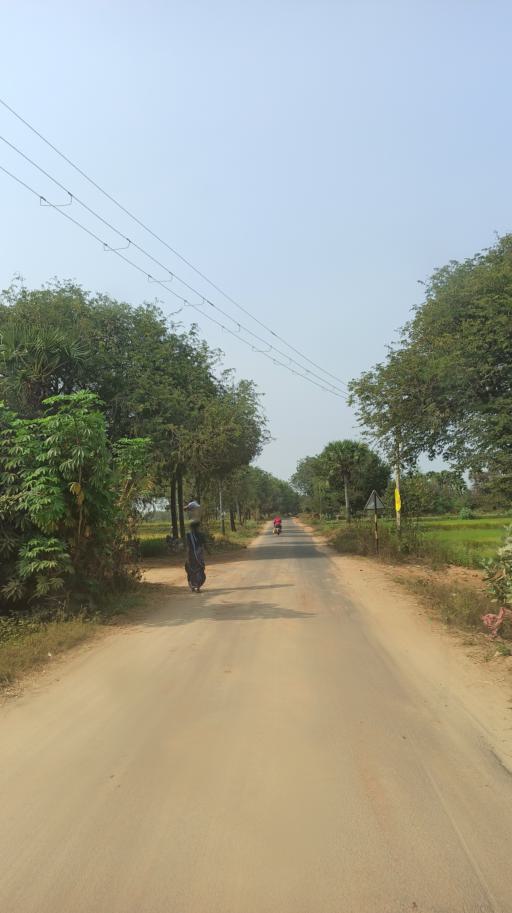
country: IN
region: Tamil Nadu
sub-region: Tiruvannamalai
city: Desur
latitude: 12.4560
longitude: 79.3722
